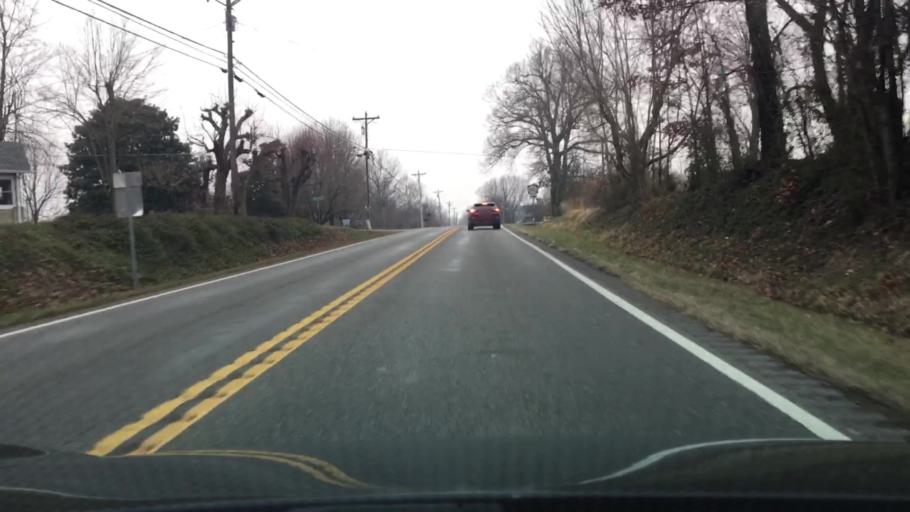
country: US
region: Kentucky
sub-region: Livingston County
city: Ledbetter
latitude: 36.9725
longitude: -88.4663
